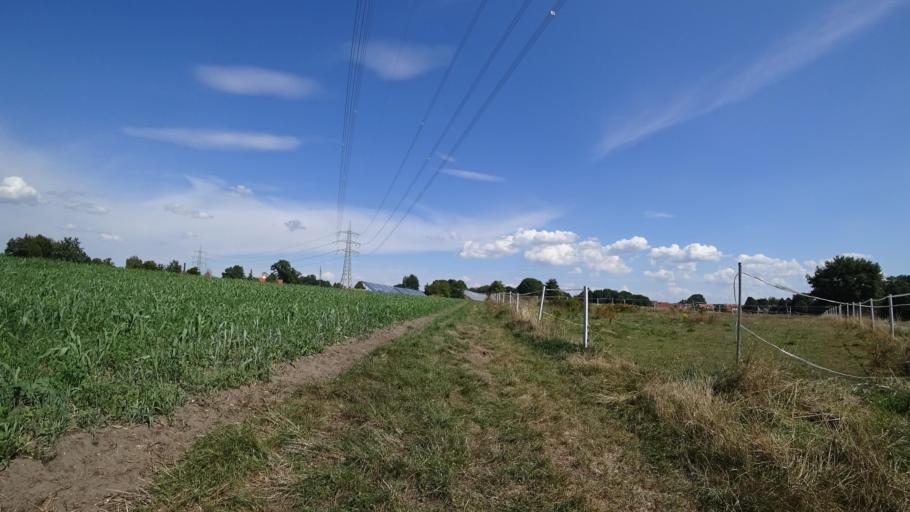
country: DE
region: North Rhine-Westphalia
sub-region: Regierungsbezirk Detmold
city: Steinhagen
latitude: 51.9539
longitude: 8.3909
